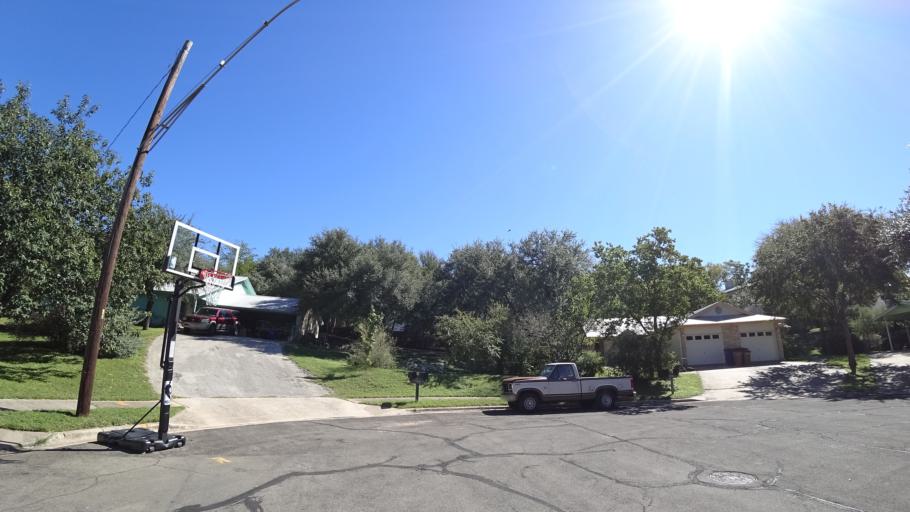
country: US
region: Texas
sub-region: Travis County
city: Austin
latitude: 30.2317
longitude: -97.7683
